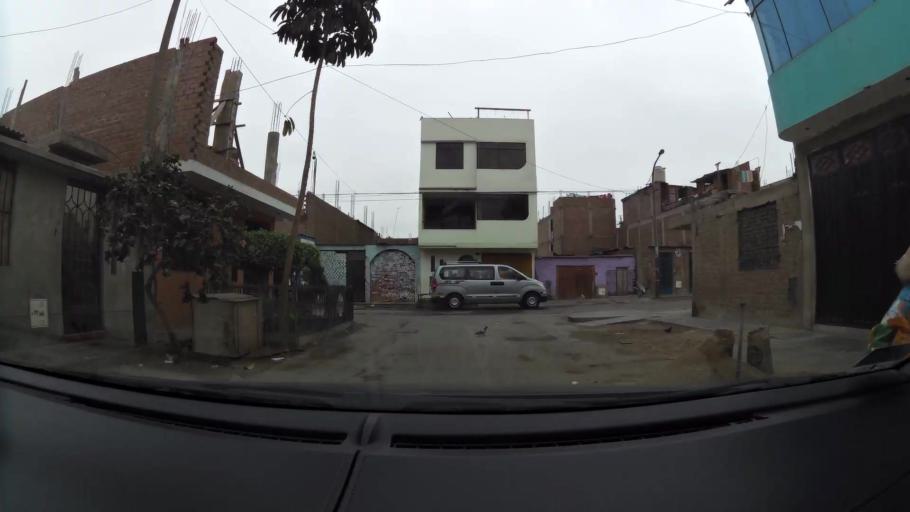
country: PE
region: Lima
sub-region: Lima
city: Independencia
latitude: -11.9652
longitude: -77.0768
